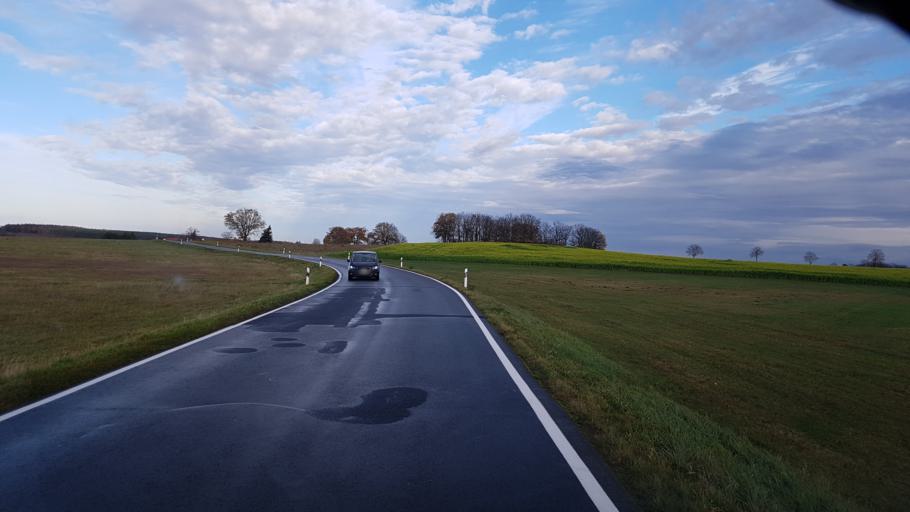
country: DE
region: Brandenburg
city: Ortrand
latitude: 51.3353
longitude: 13.7607
